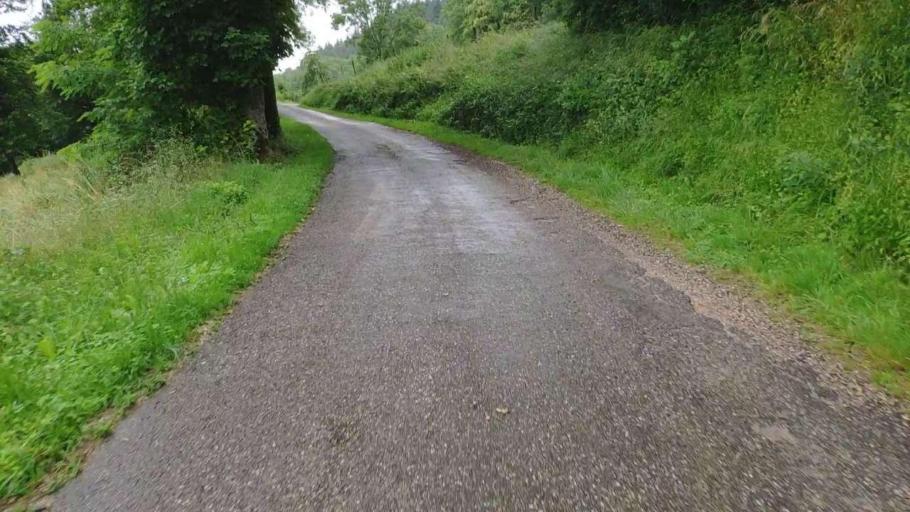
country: FR
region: Franche-Comte
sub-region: Departement du Jura
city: Poligny
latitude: 46.7884
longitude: 5.6207
